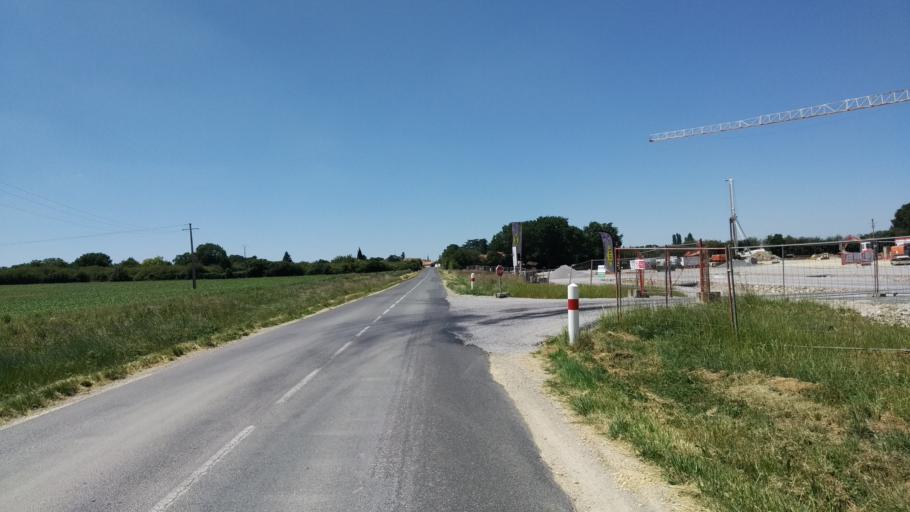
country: FR
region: Poitou-Charentes
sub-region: Departement de la Vienne
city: Biard
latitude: 46.5999
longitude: 0.2915
